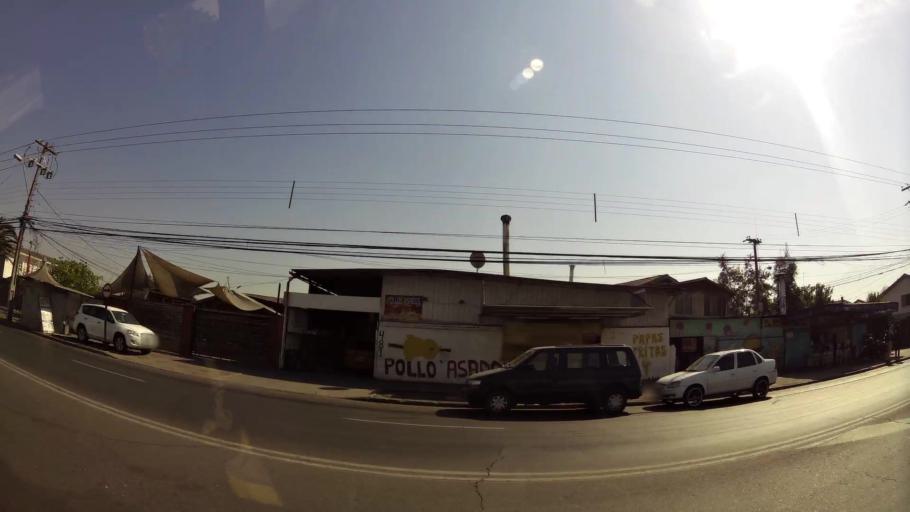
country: CL
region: Santiago Metropolitan
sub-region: Provincia de Santiago
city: La Pintana
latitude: -33.5471
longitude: -70.5927
